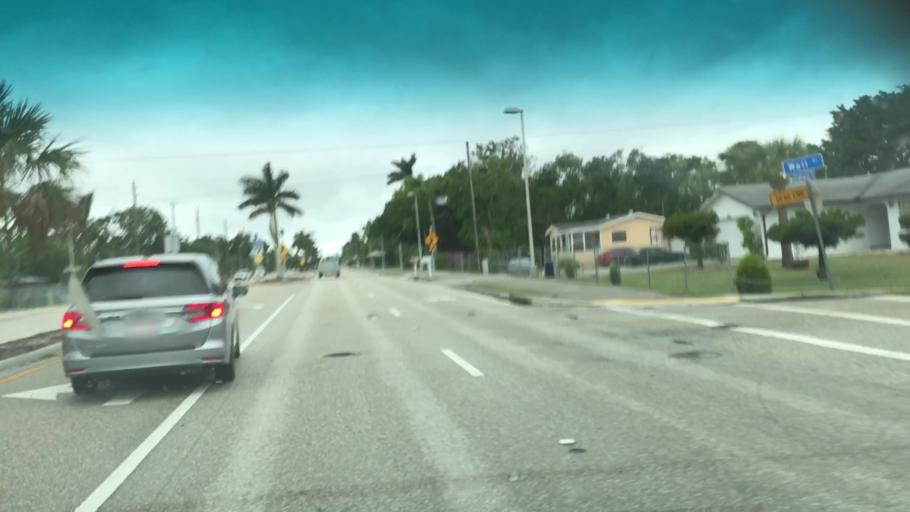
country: US
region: Florida
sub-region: Lee County
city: Harlem Heights
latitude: 26.5183
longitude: -81.9292
